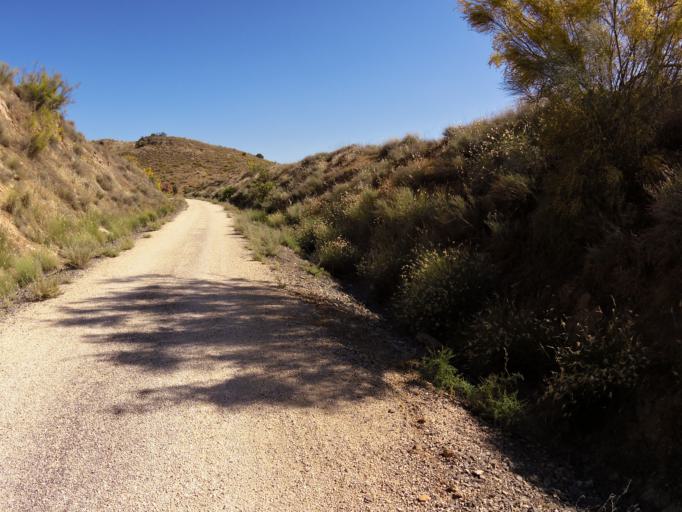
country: ES
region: Andalusia
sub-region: Provincia de Jaen
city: Alcaudete
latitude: 37.5969
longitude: -4.1559
